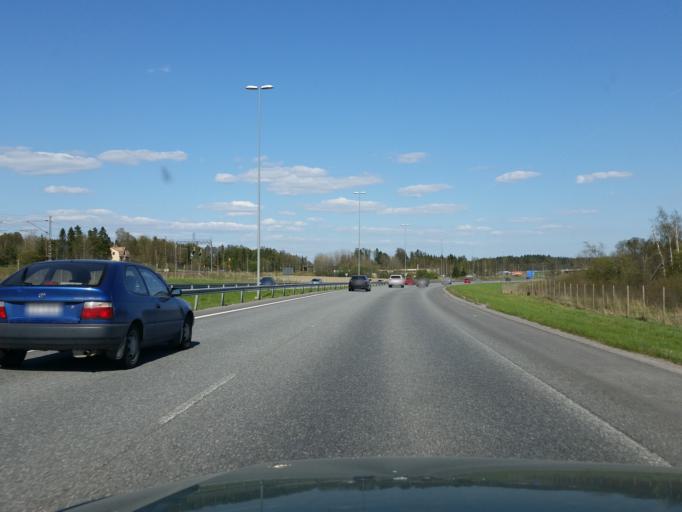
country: FI
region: Uusimaa
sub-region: Helsinki
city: Kirkkonummi
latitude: 60.1307
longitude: 24.4972
